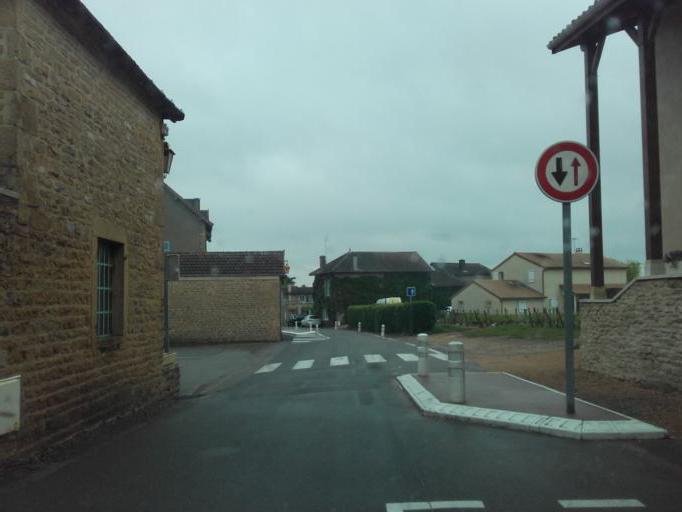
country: FR
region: Bourgogne
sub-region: Departement de Saone-et-Loire
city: Creches-sur-Saone
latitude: 46.2514
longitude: 4.7561
